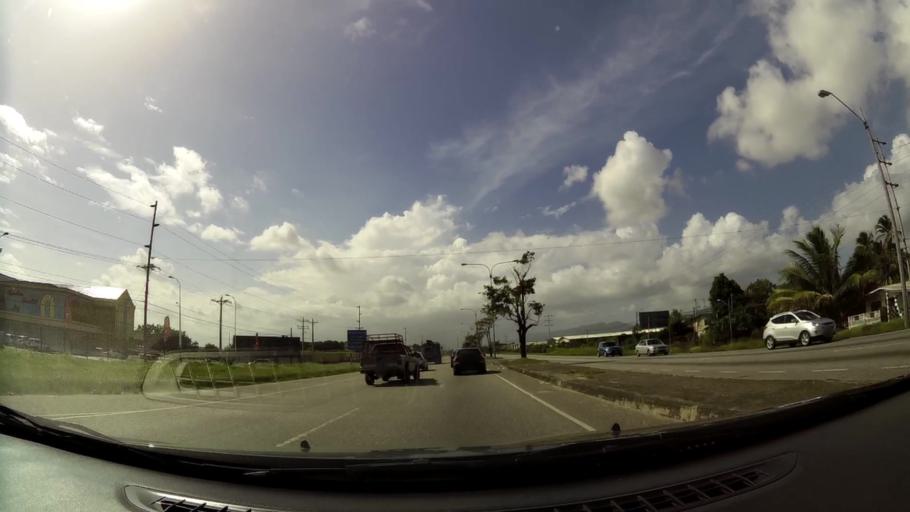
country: TT
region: Borough of Arima
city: Arima
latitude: 10.6102
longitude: -61.2925
